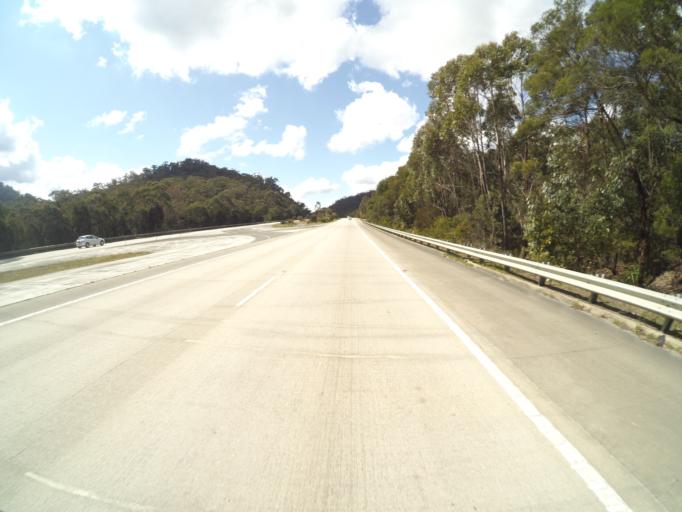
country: AU
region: New South Wales
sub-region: Wingecarribee
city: Mittagong
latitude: -34.4324
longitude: 150.4531
